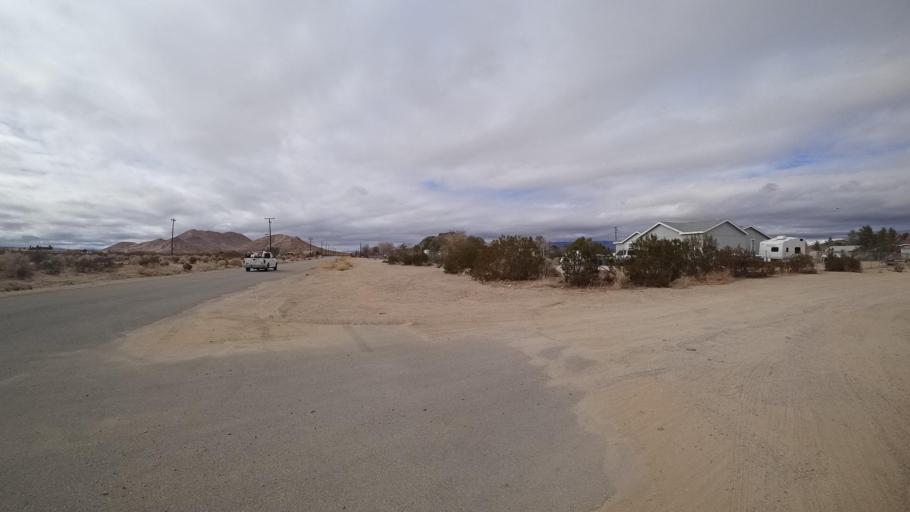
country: US
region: California
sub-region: Kern County
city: Rosamond
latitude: 34.8929
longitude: -118.2403
